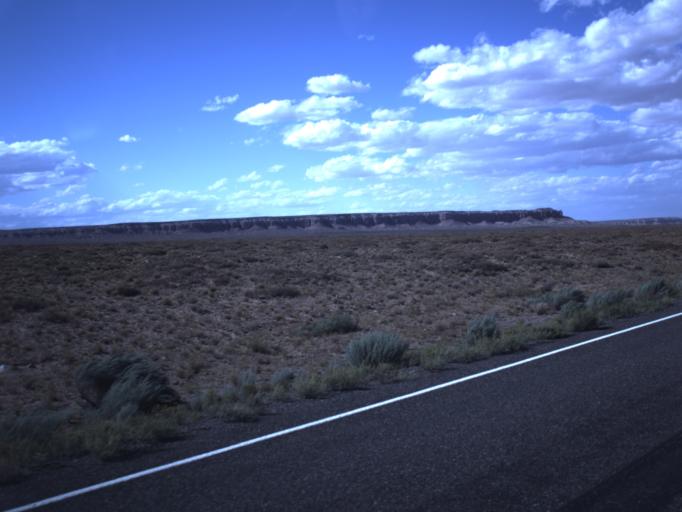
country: US
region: Utah
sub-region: Wayne County
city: Loa
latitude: 38.1814
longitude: -110.6261
